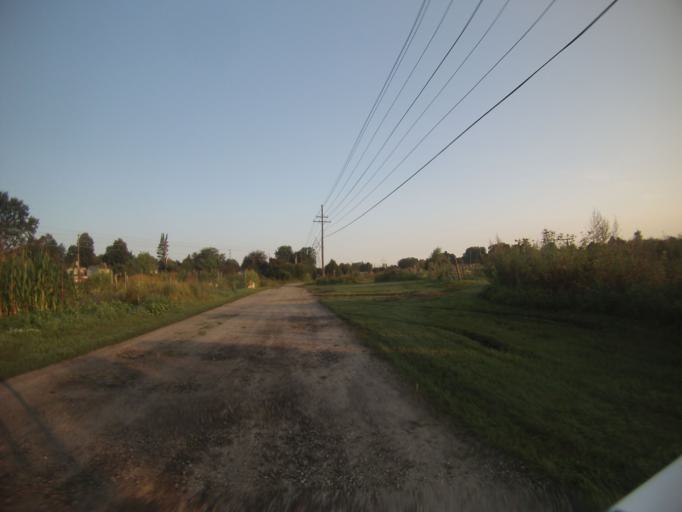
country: CA
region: Ontario
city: Ottawa
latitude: 45.3898
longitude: -75.6391
